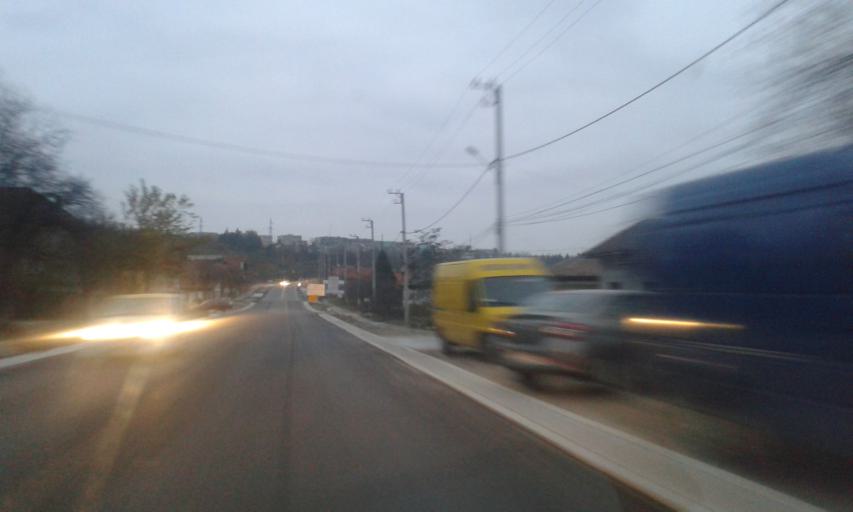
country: RO
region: Gorj
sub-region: Comuna Bumbesti-Jiu
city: Bumbesti-Jiu
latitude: 45.1860
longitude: 23.3866
